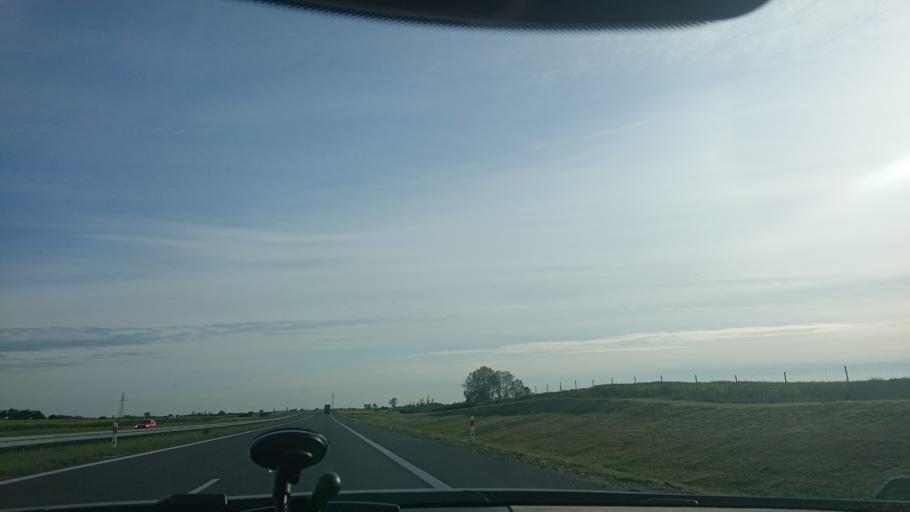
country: PL
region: Greater Poland Voivodeship
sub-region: Powiat gnieznienski
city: Gniezno
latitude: 52.5373
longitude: 17.5222
